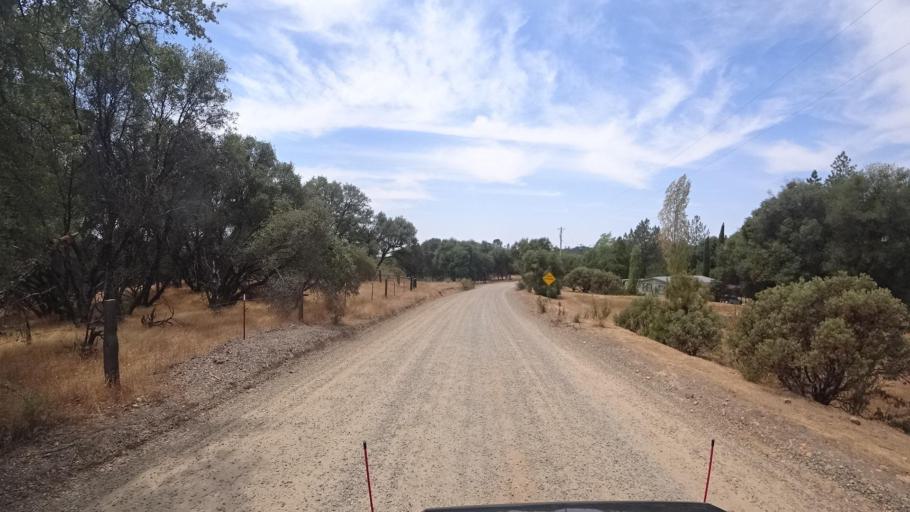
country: US
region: California
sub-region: Madera County
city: Ahwahnee
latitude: 37.4433
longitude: -119.8176
